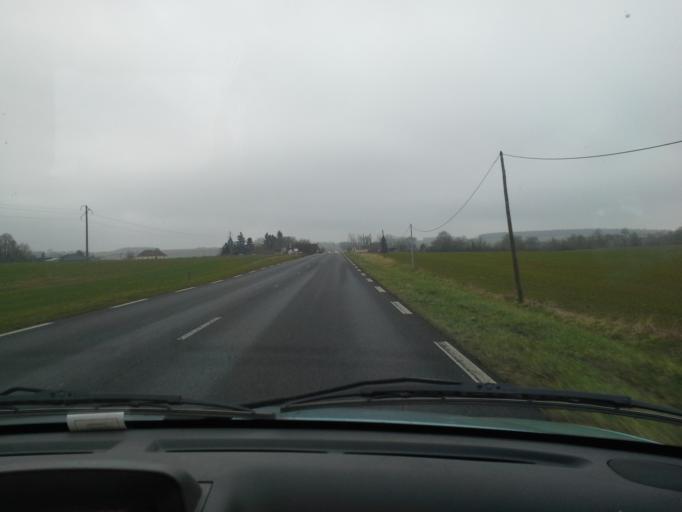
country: FR
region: Centre
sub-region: Departement du Loir-et-Cher
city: Saint-Amand-Longpre
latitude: 47.6522
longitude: 0.9551
